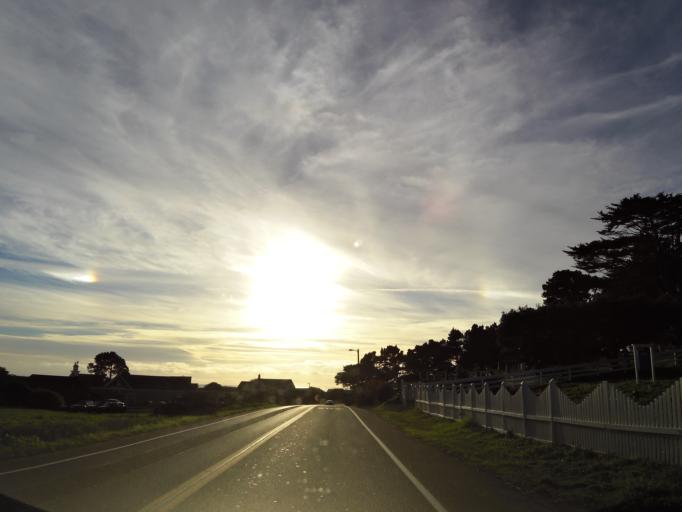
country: US
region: California
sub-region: Mendocino County
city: Fort Bragg
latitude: 39.3087
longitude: -123.7974
